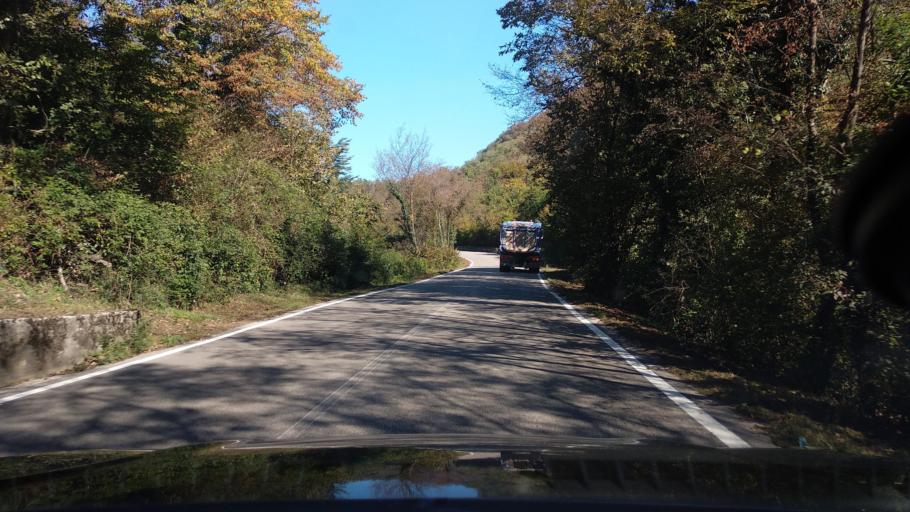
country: IT
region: Veneto
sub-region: Provincia di Verona
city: Torri del Benaco
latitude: 45.5956
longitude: 10.6996
